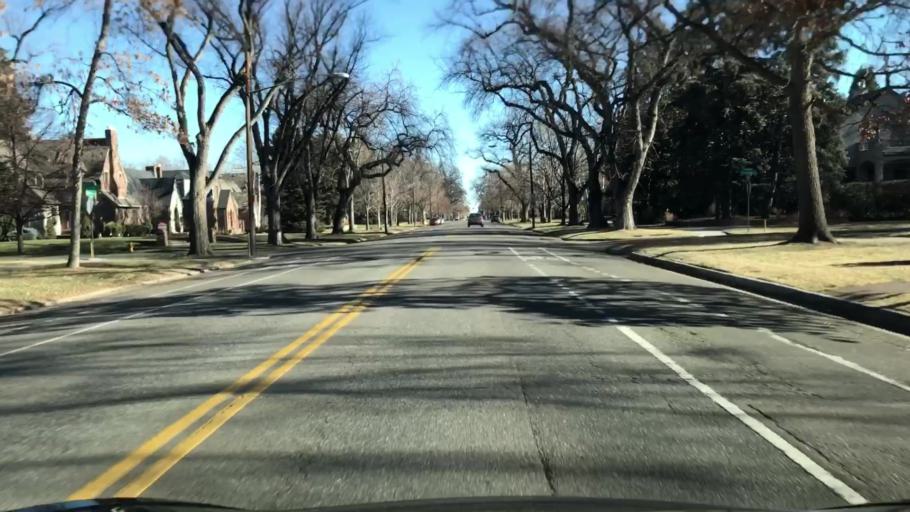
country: US
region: Colorado
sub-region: Arapahoe County
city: Glendale
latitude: 39.7474
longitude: -104.9180
